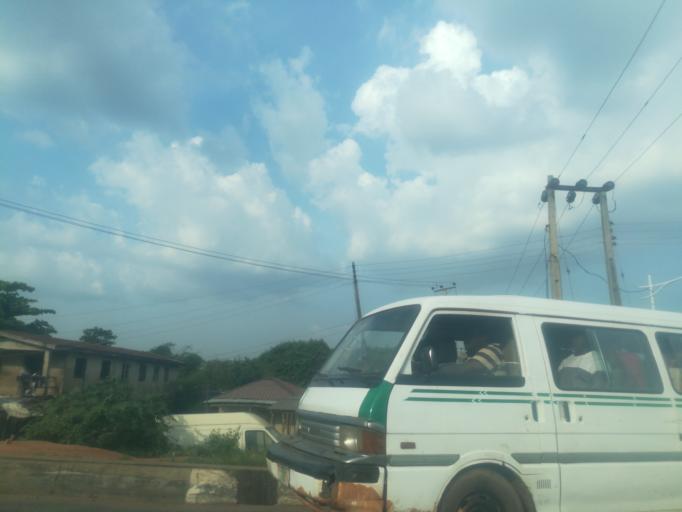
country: NG
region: Ogun
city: Abeokuta
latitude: 7.1467
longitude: 3.3275
